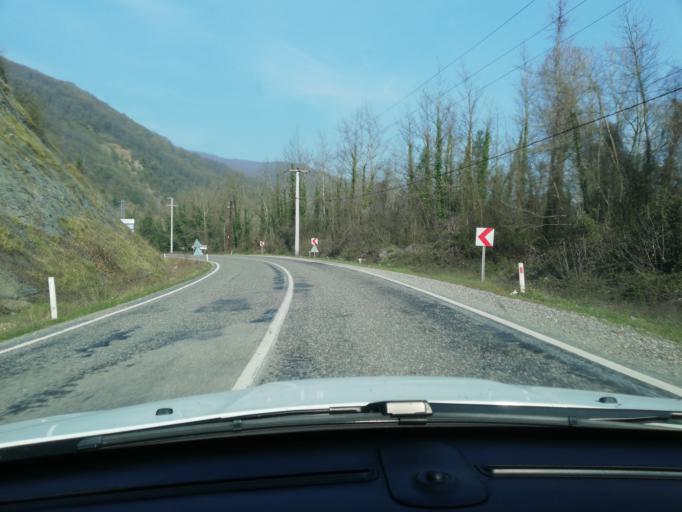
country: TR
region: Karabuk
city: Yenice
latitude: 41.2036
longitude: 32.3708
